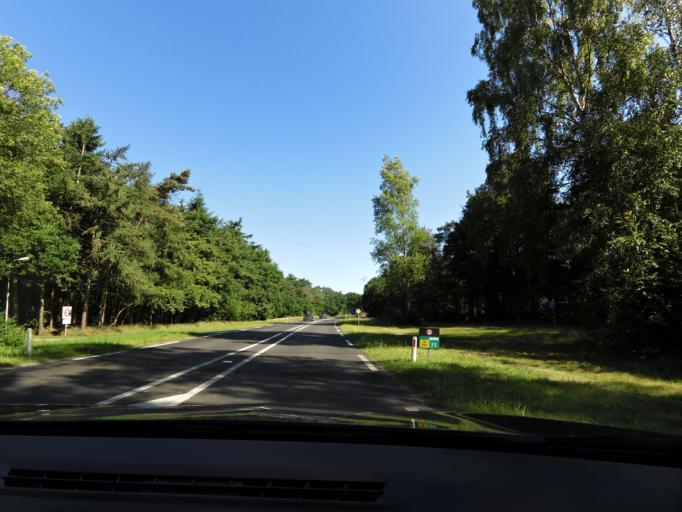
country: NL
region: Overijssel
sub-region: Gemeente Twenterand
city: Den Ham
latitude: 52.4926
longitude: 6.4237
